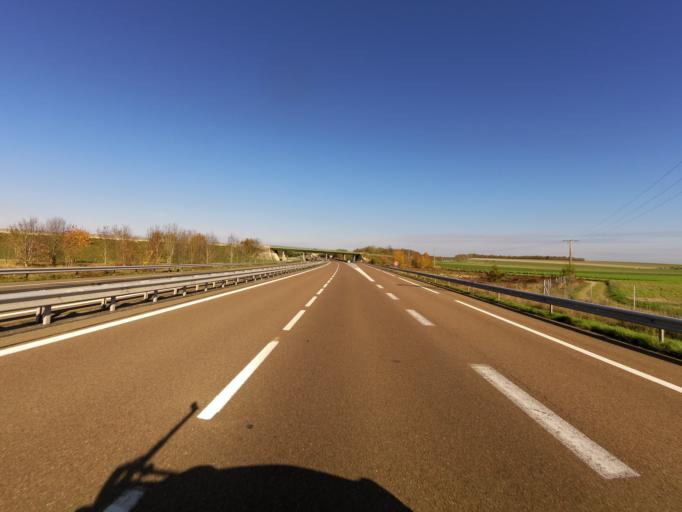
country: FR
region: Champagne-Ardenne
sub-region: Departement de la Marne
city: Compertrix
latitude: 48.8810
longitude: 4.2902
